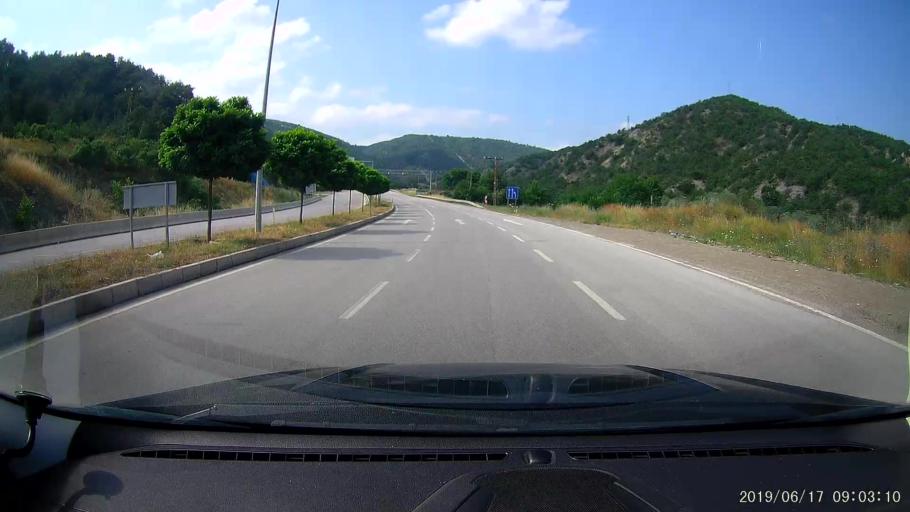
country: TR
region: Amasya
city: Tasova
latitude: 40.7589
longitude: 36.3023
